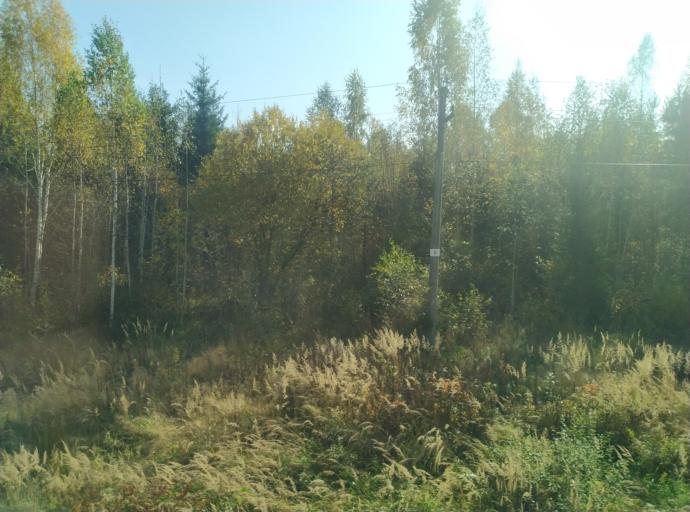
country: RU
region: Moskovskaya
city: Novo-Nikol'skoye
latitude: 56.5441
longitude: 37.5509
